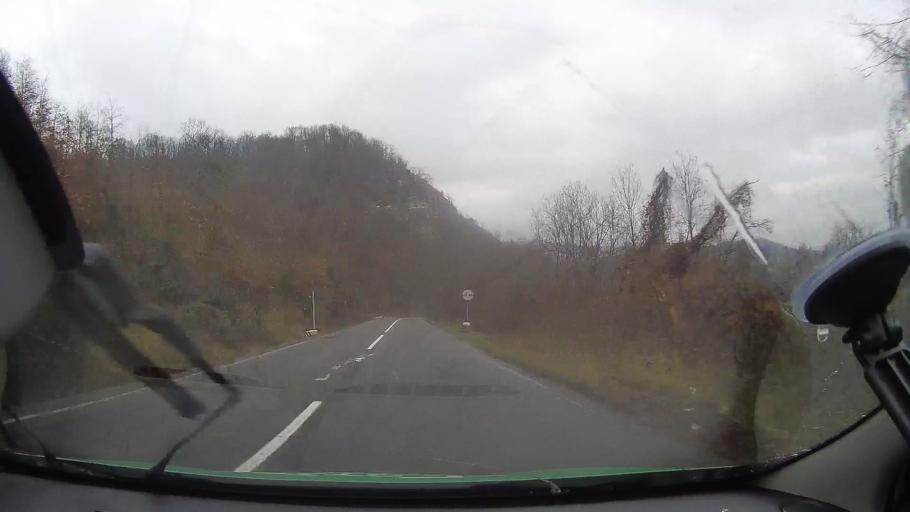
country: RO
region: Arad
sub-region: Comuna Gurahont
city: Gurahont
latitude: 46.2761
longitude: 22.3488
